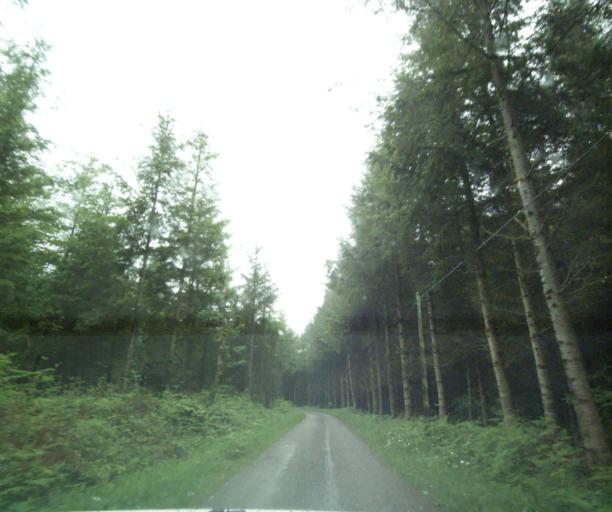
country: FR
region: Bourgogne
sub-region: Departement de Saone-et-Loire
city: La Clayette
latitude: 46.3705
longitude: 4.3665
